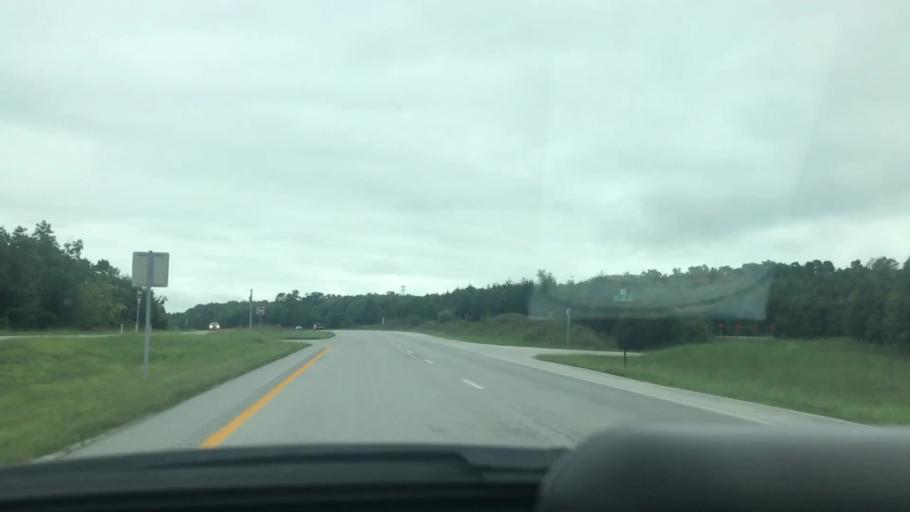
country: US
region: Missouri
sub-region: Greene County
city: Fair Grove
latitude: 37.3183
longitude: -93.1690
